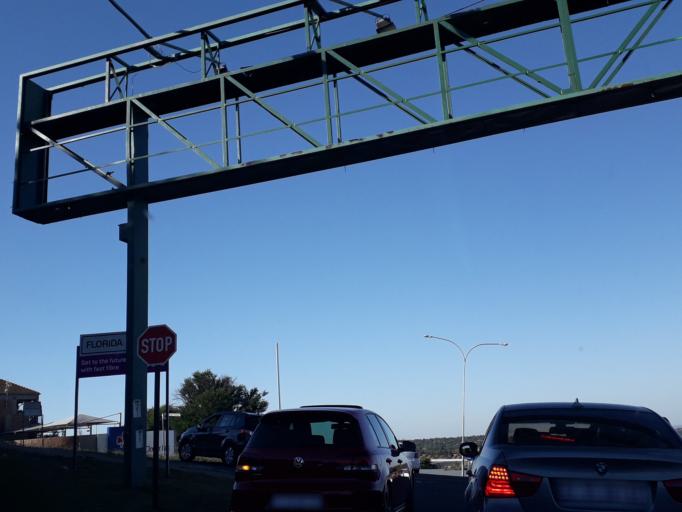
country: ZA
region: Gauteng
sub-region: City of Johannesburg Metropolitan Municipality
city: Roodepoort
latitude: -26.1463
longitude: 27.9203
